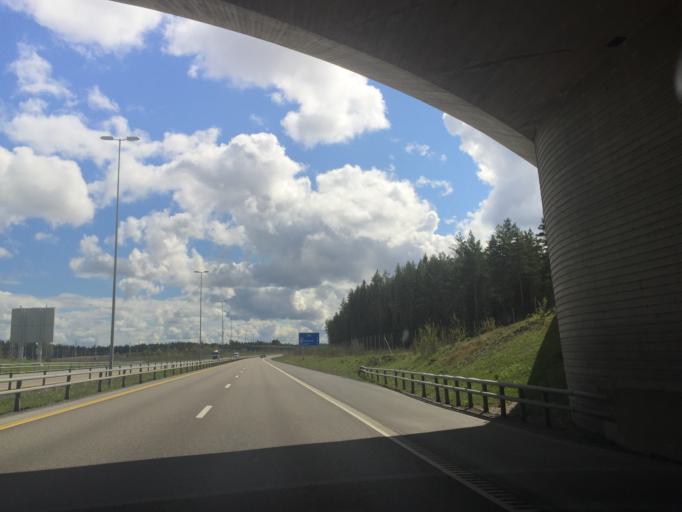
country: NO
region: Akershus
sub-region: Eidsvoll
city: Raholt
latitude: 60.2235
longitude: 11.1771
